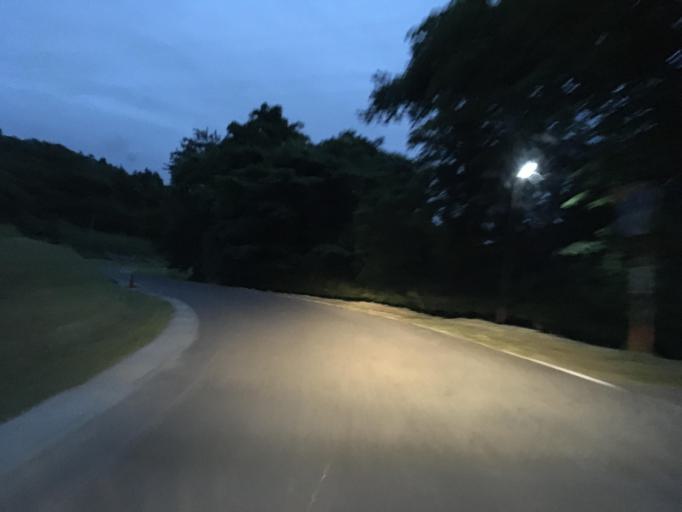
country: JP
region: Miyagi
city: Furukawa
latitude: 38.7863
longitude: 140.9397
